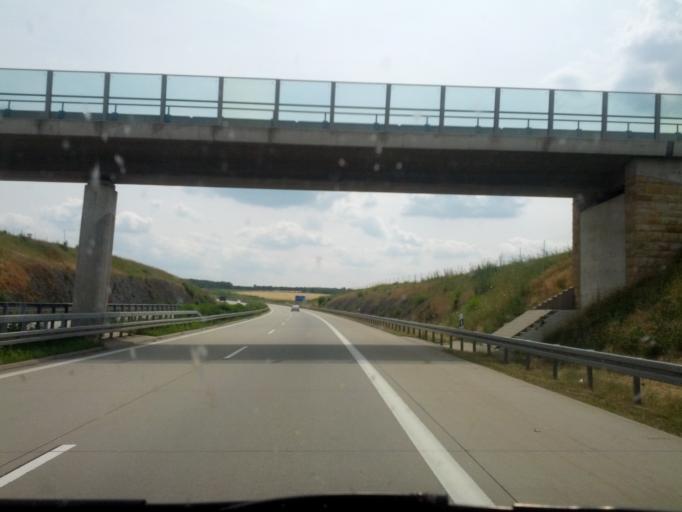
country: DE
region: Saxony
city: Liebstadt
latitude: 50.8077
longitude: 13.8808
